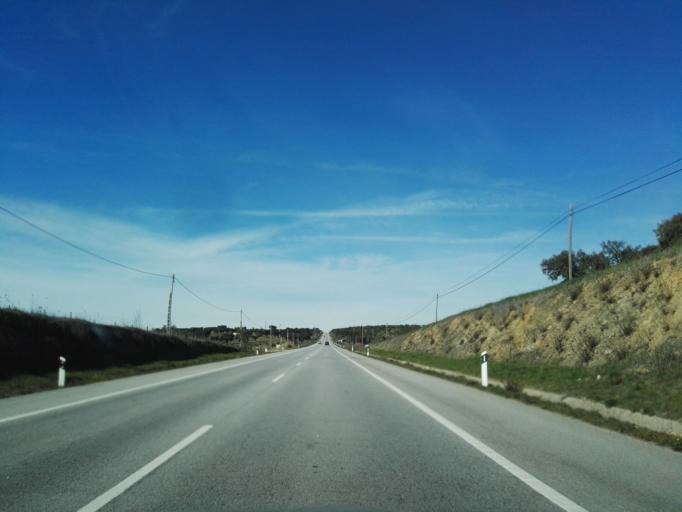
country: PT
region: Portalegre
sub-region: Arronches
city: Arronches
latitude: 39.1388
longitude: -7.2961
